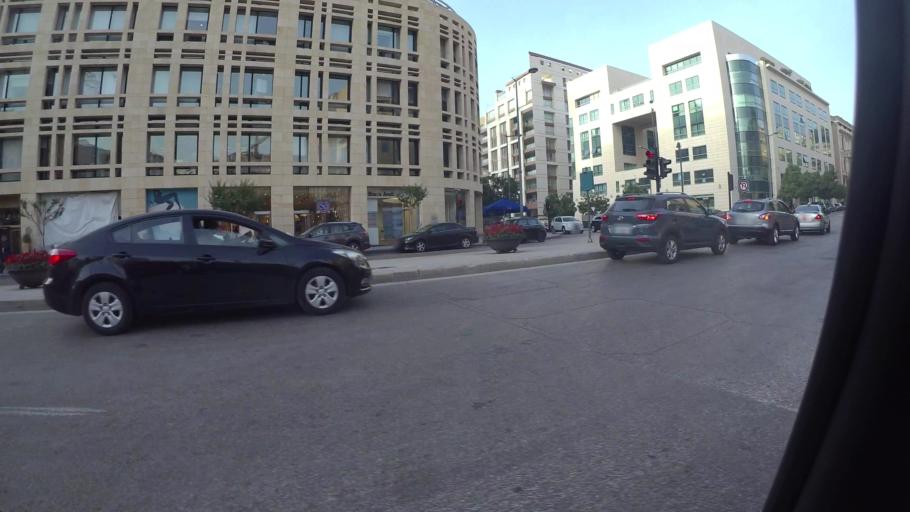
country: LB
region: Beyrouth
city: Beirut
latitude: 33.8987
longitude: 35.5010
